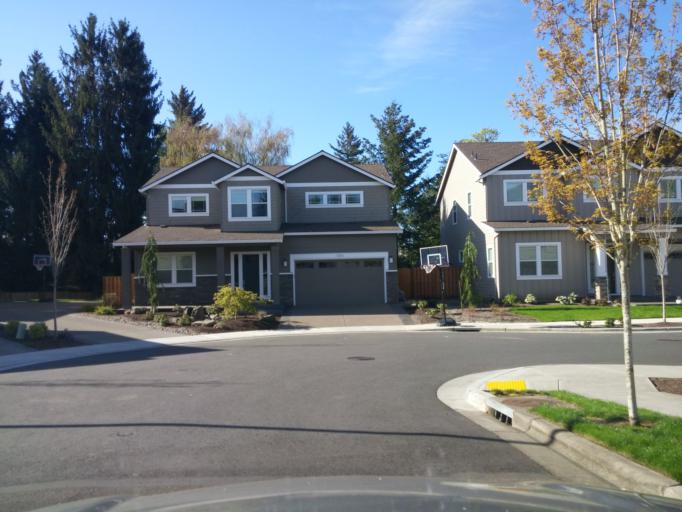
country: US
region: Oregon
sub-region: Washington County
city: Cedar Mill
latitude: 45.5346
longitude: -122.7934
